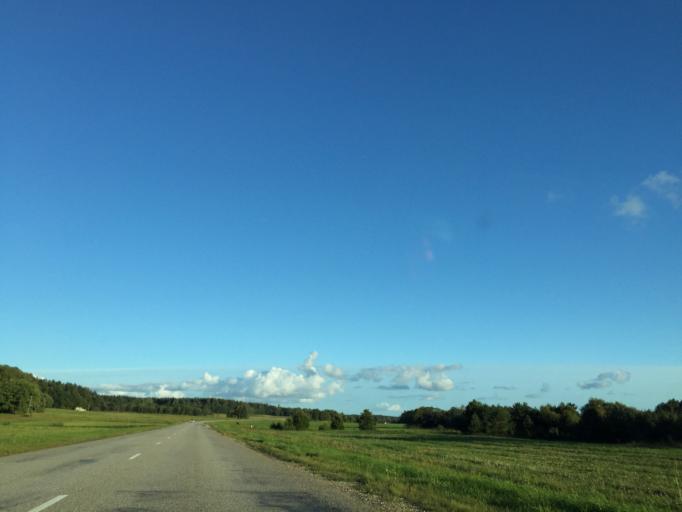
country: LV
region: Kuldigas Rajons
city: Kuldiga
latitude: 56.9298
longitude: 22.0439
